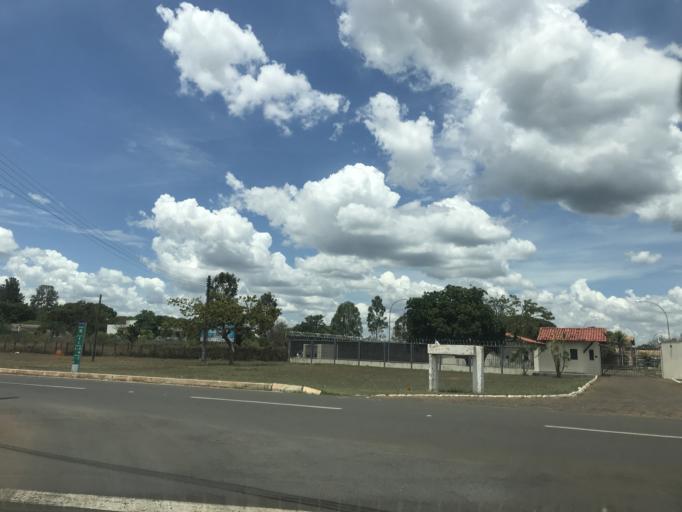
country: BR
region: Federal District
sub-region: Brasilia
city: Brasilia
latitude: -15.9093
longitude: -47.9464
